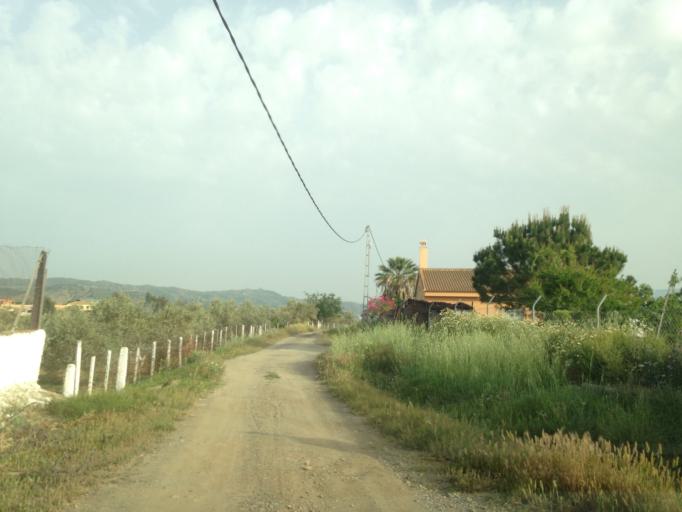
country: ES
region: Andalusia
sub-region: Provincia de Malaga
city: Estacion de Cartama
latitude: 36.7528
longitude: -4.5527
